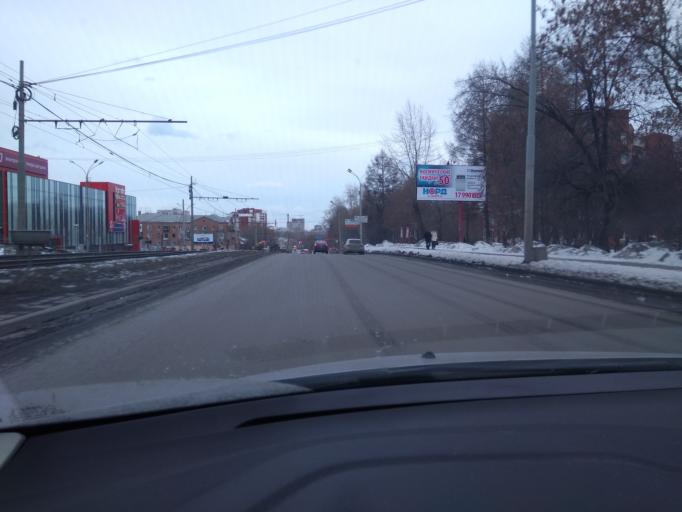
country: RU
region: Sverdlovsk
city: Yekaterinburg
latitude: 56.8526
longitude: 60.6385
